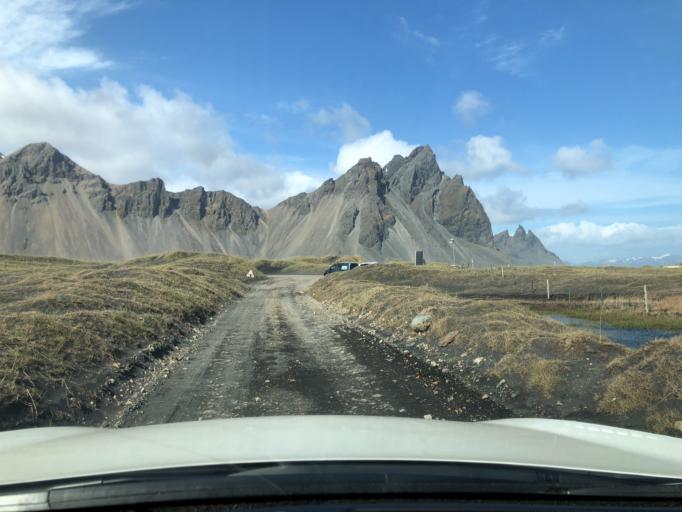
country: IS
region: East
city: Hoefn
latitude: 64.2434
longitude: -14.9716
